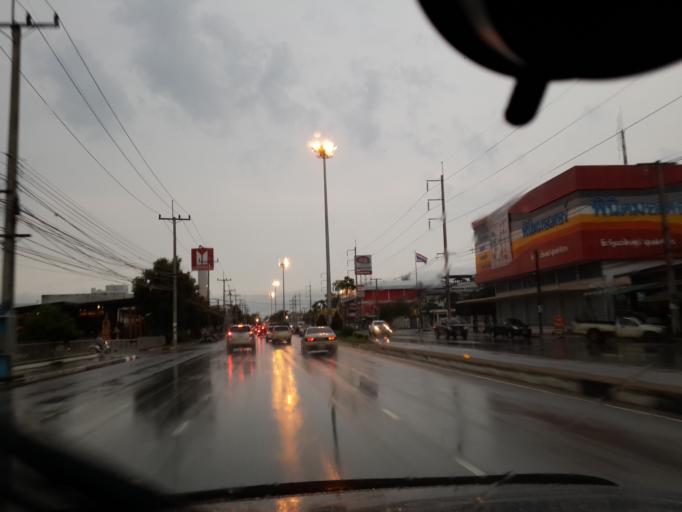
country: TH
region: Yala
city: Yala
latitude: 6.5511
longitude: 101.2731
